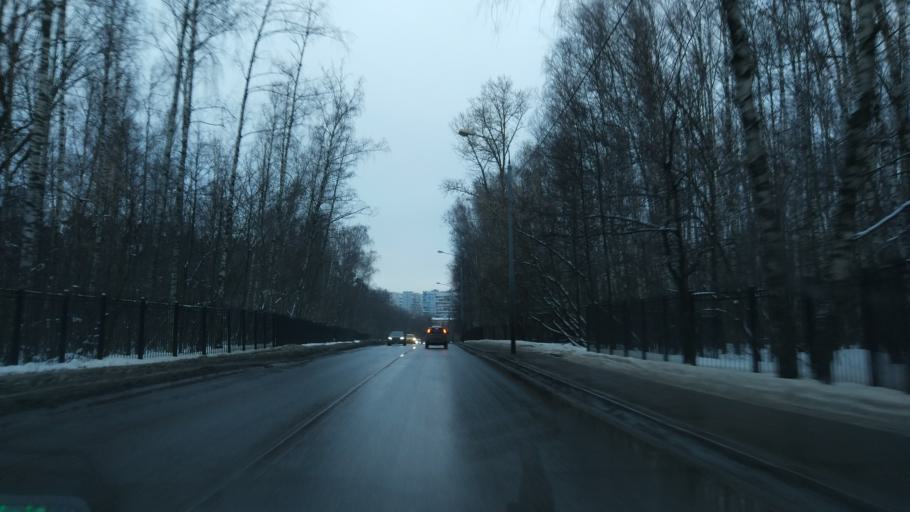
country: RU
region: Moskovskaya
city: Izmaylovo
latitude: 55.7857
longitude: 37.8197
